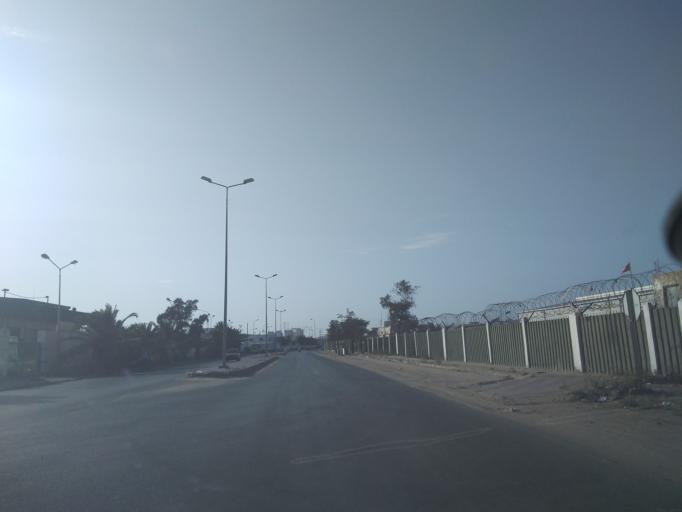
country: TN
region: Safaqis
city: Sfax
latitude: 34.7239
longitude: 10.7579
